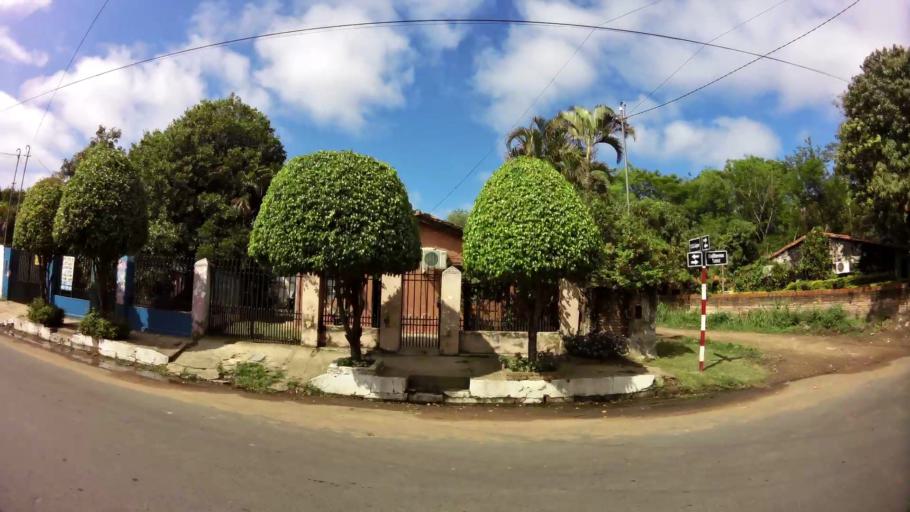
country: PY
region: Central
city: San Lorenzo
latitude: -25.2791
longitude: -57.4949
